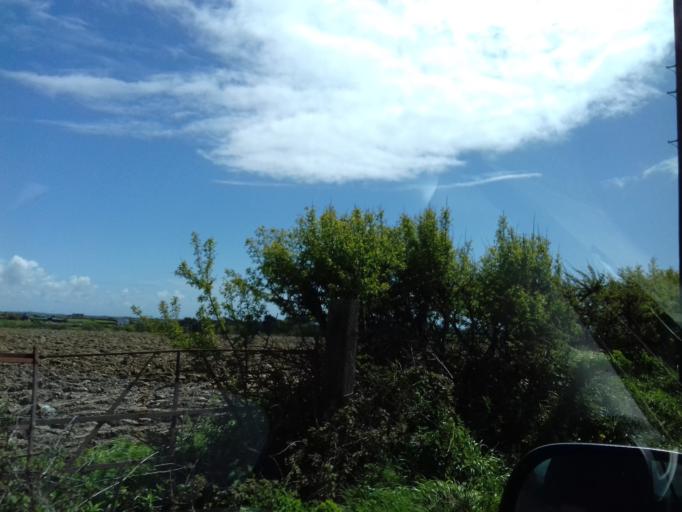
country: IE
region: Munster
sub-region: Waterford
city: Dunmore East
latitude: 52.2192
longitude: -6.8604
